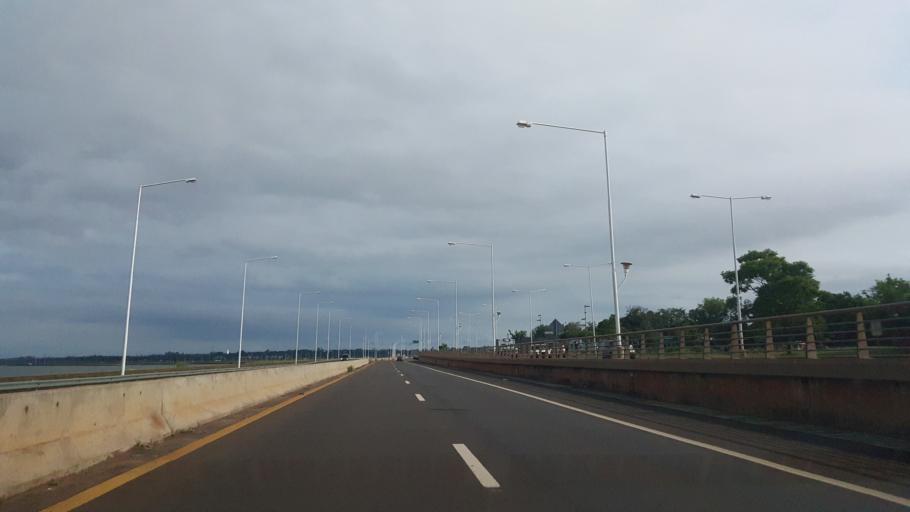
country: AR
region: Misiones
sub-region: Departamento de Capital
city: Posadas
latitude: -27.3999
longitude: -55.8921
